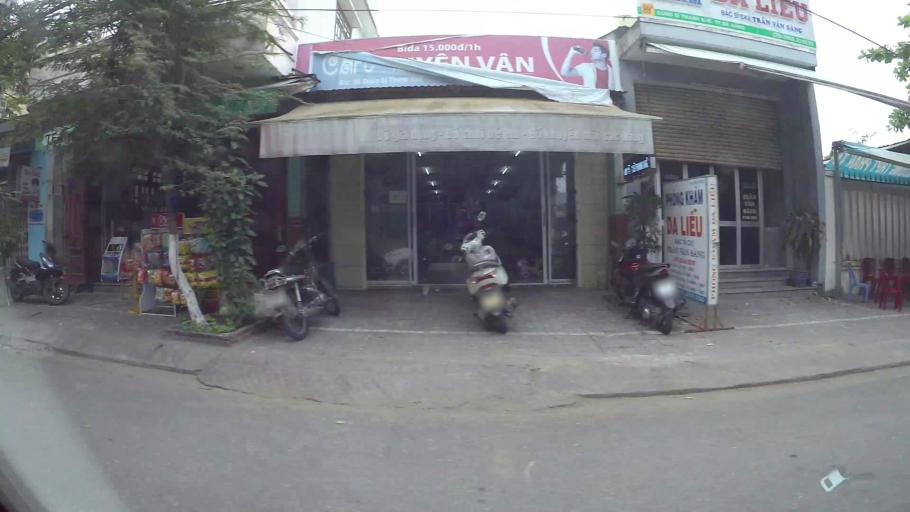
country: VN
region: Da Nang
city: Thanh Khe
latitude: 16.0740
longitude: 108.1769
